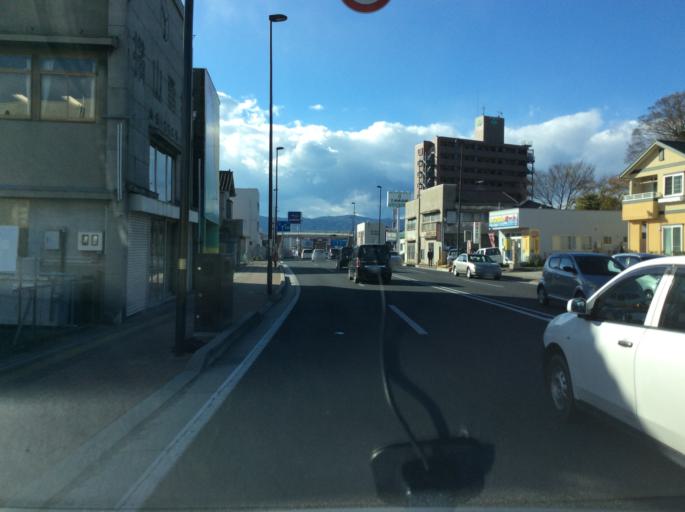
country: JP
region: Fukushima
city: Iwaki
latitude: 37.0533
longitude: 140.8839
